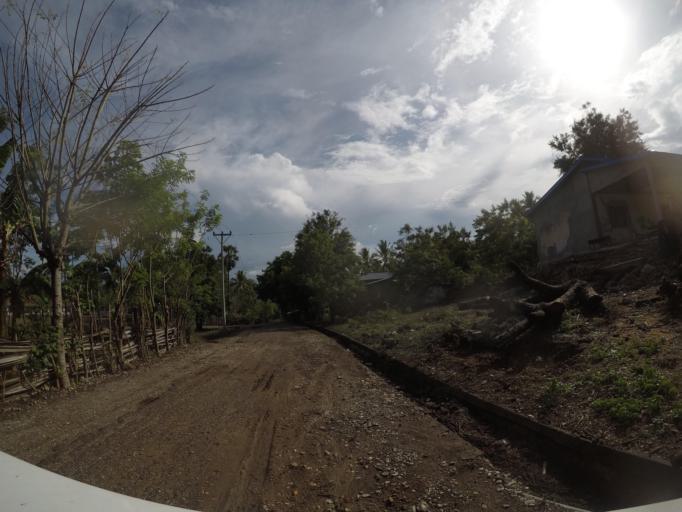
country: TL
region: Baucau
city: Baucau
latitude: -8.5037
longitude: 126.4644
